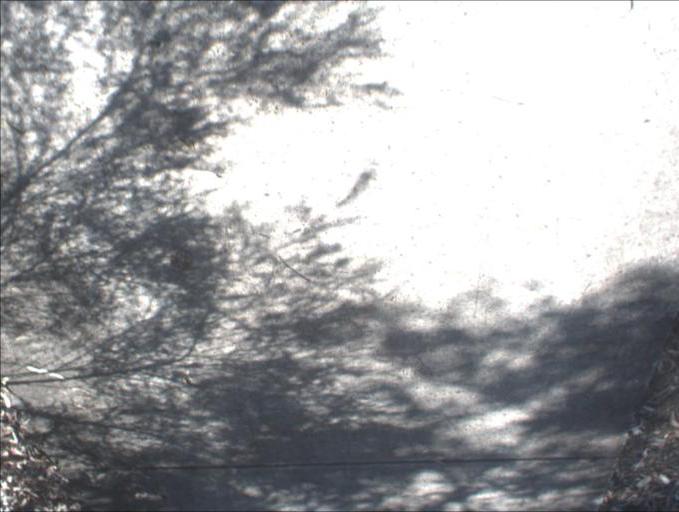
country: AU
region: Queensland
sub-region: Logan
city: Windaroo
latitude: -27.7578
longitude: 153.1862
